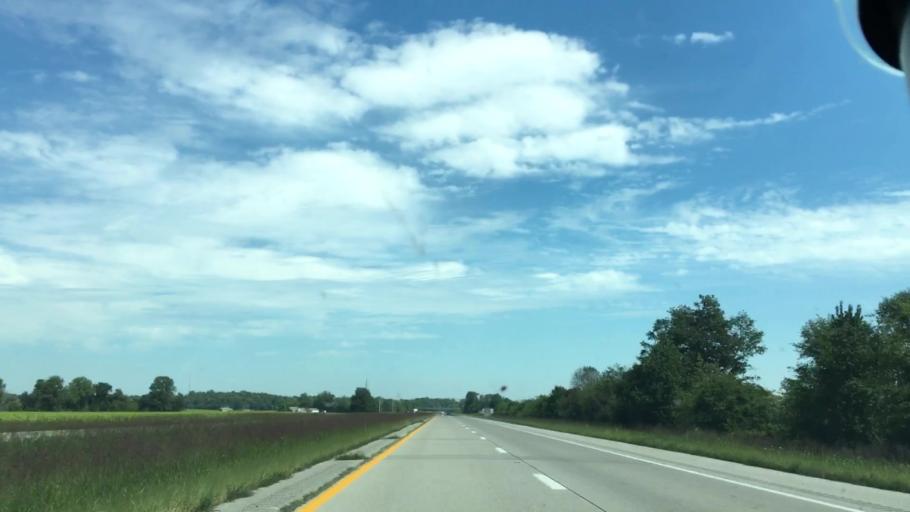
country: US
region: Kentucky
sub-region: Daviess County
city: Owensboro
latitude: 37.7625
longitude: -87.2243
